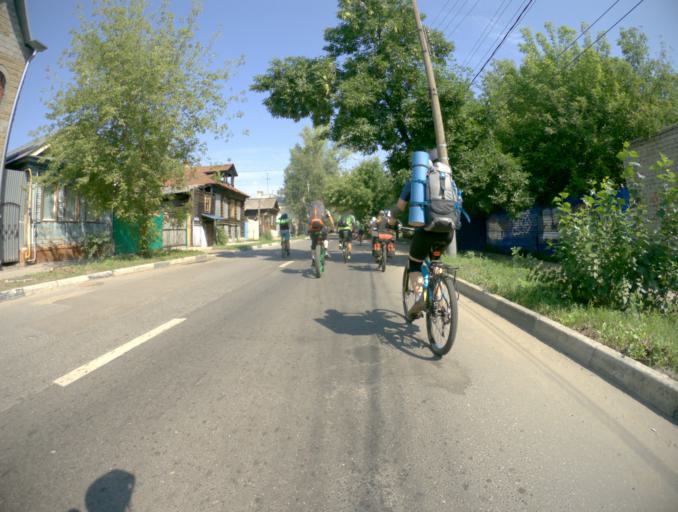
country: RU
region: Nizjnij Novgorod
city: Nizhniy Novgorod
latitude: 56.3167
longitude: 43.9515
